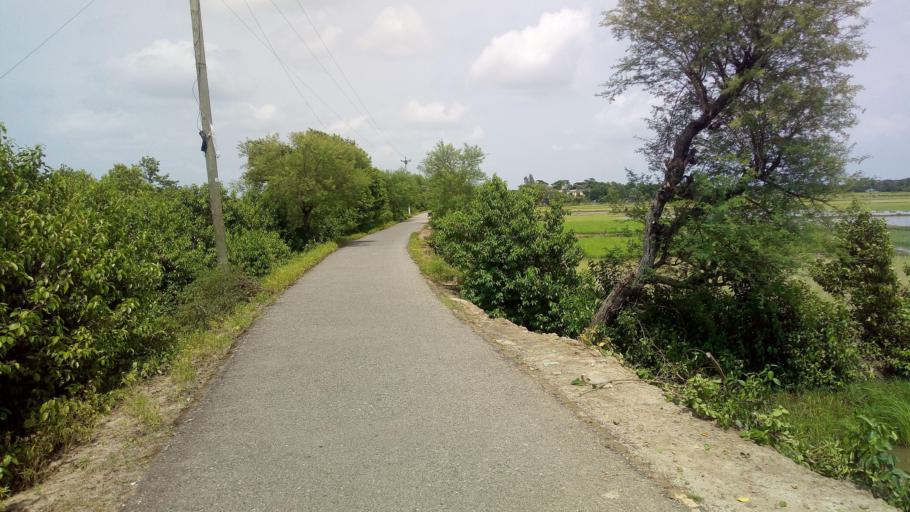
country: BD
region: Khulna
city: Phultala
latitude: 22.5716
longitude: 89.4495
